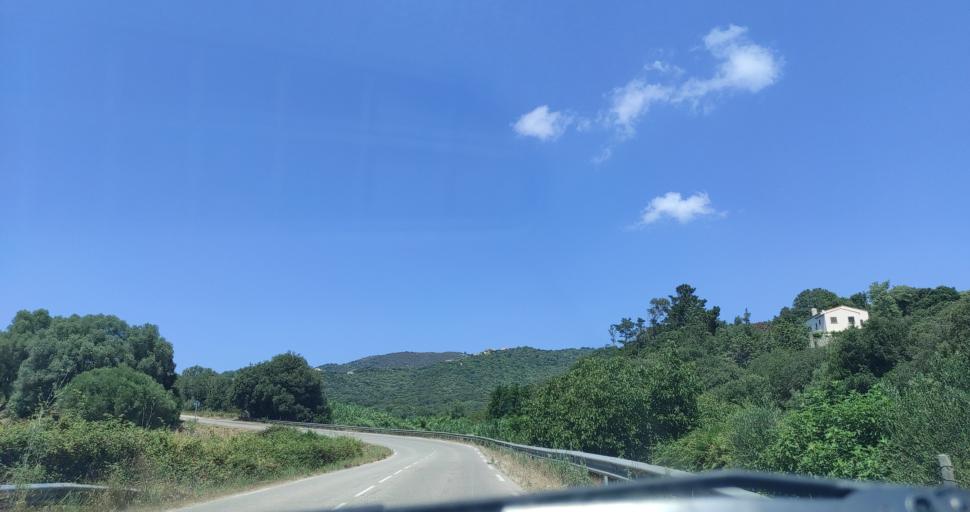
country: FR
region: Corsica
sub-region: Departement de la Corse-du-Sud
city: Ajaccio
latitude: 41.9524
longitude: 8.7322
